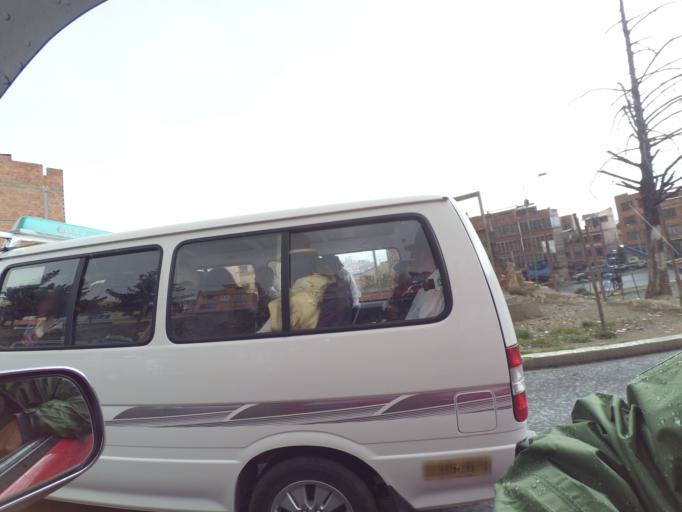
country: BO
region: La Paz
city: La Paz
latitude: -16.4929
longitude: -68.1650
